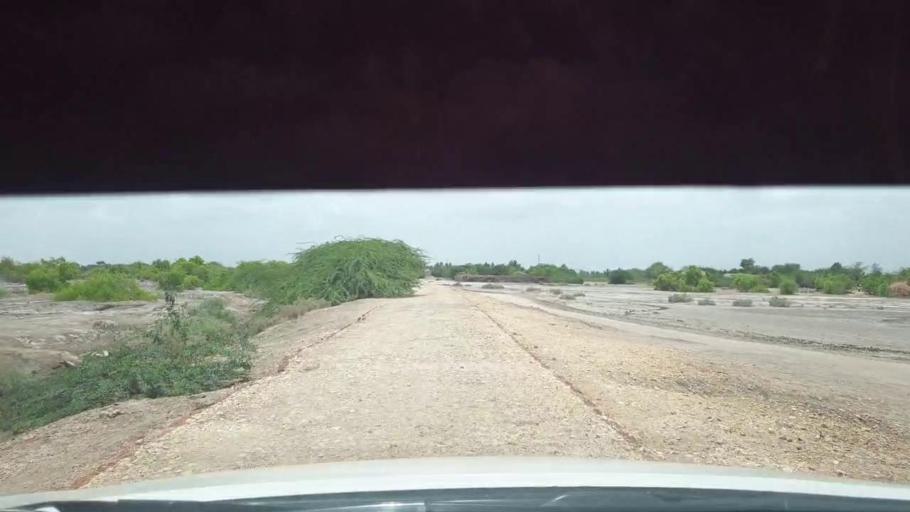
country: PK
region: Sindh
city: Kadhan
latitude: 24.4864
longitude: 69.0018
